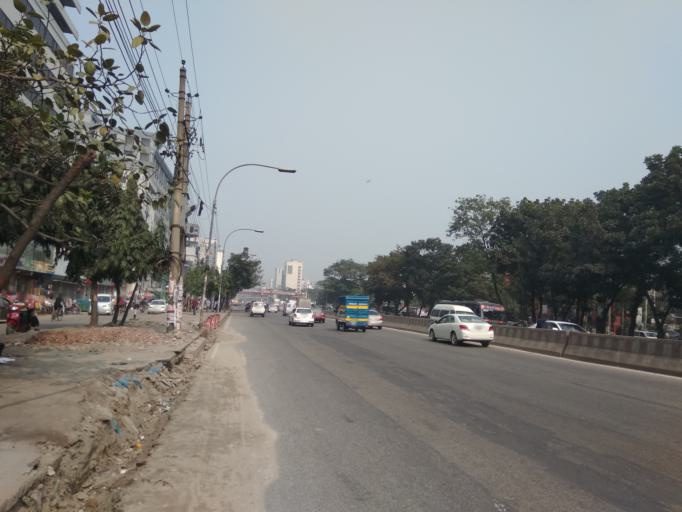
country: BD
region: Dhaka
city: Tungi
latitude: 23.8662
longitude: 90.4001
